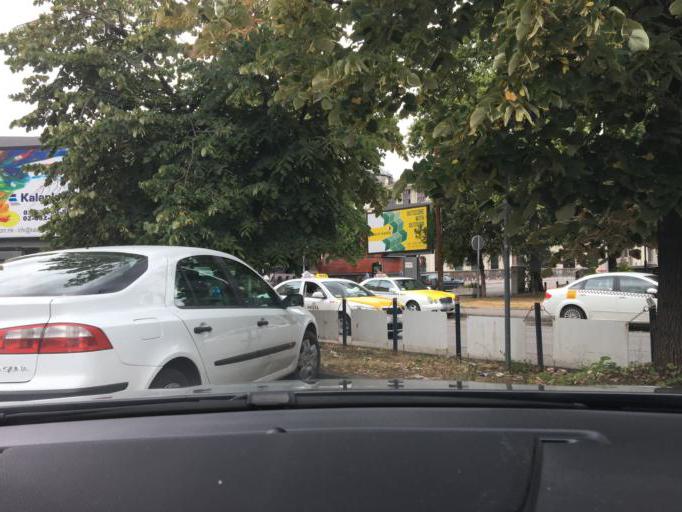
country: MK
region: Karpos
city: Skopje
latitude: 41.9945
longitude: 21.4373
